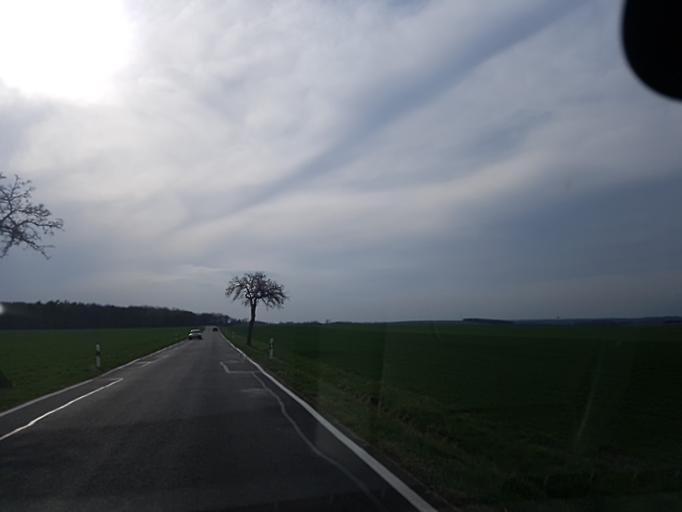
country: DE
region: Saxony
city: Cavertitz
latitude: 51.3672
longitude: 13.1795
